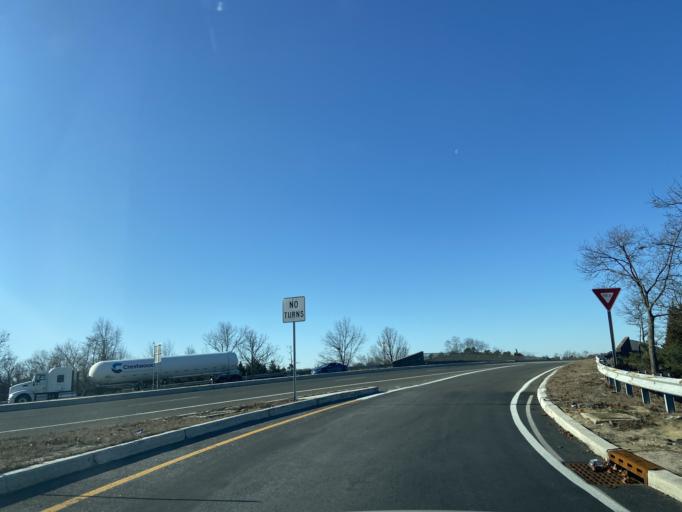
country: US
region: New Jersey
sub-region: Cumberland County
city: Vineland
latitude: 39.4885
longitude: -75.0699
